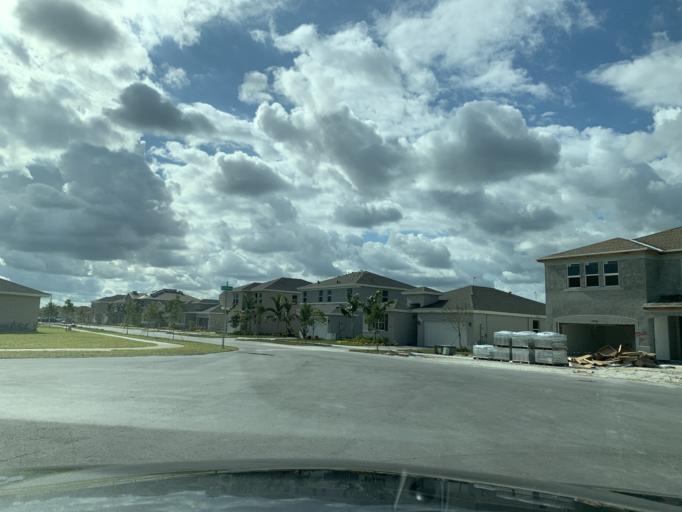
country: US
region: Florida
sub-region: Miami-Dade County
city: Naranja
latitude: 25.5120
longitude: -80.4090
